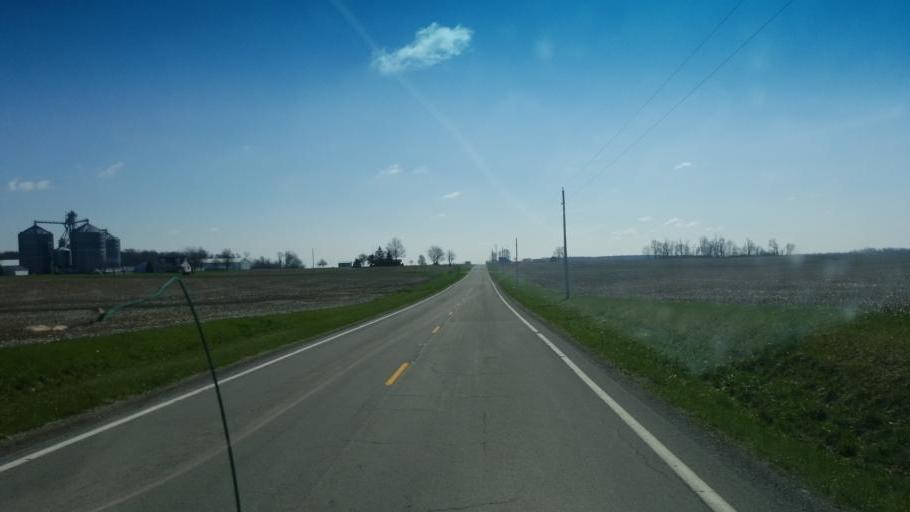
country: US
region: Ohio
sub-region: Wyandot County
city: Upper Sandusky
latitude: 40.7378
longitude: -83.3273
